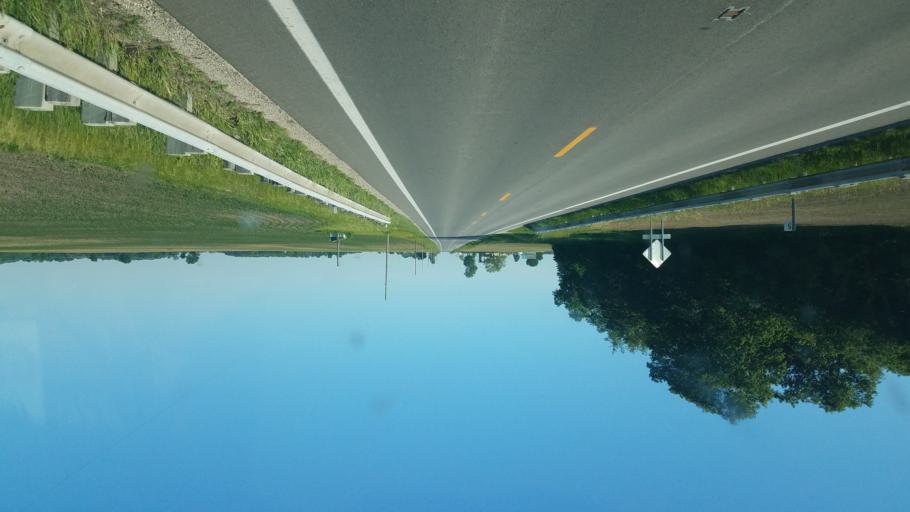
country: US
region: Ohio
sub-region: Crawford County
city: Bucyrus
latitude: 40.7741
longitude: -82.9833
